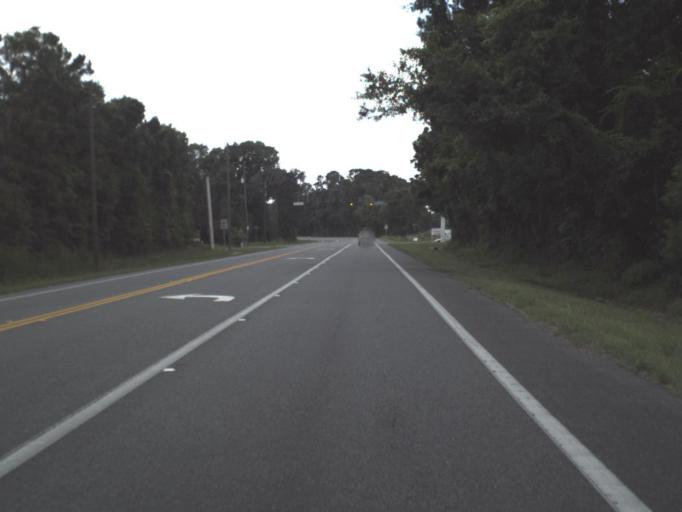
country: US
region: Florida
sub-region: Alachua County
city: Alachua
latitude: 29.8020
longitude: -82.3850
